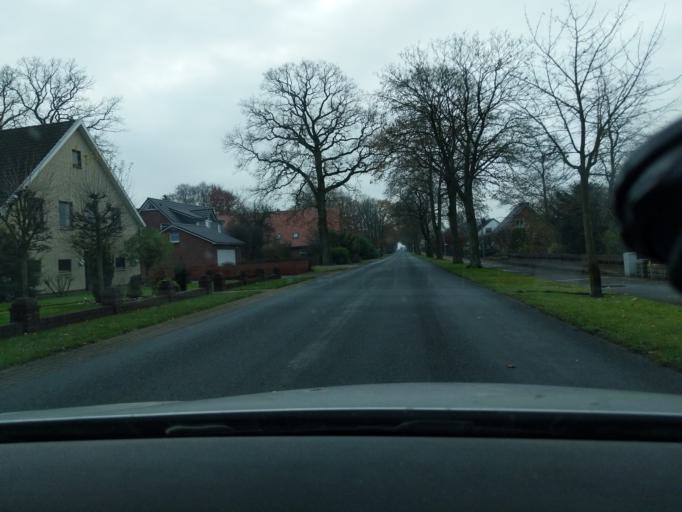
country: DE
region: Lower Saxony
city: Ahlerstedt
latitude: 53.3981
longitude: 9.4896
